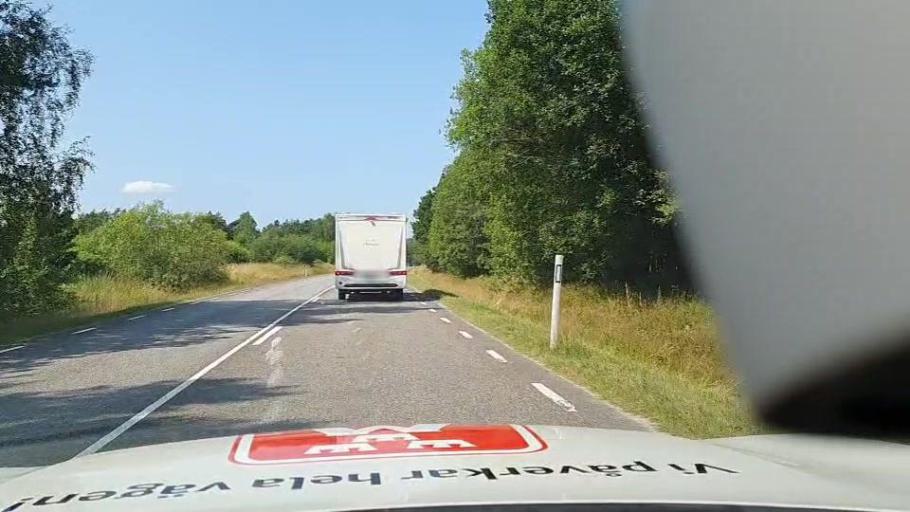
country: SE
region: Vaestra Goetaland
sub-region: Stenungsunds Kommun
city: Stora Hoga
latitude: 58.0601
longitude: 11.9104
